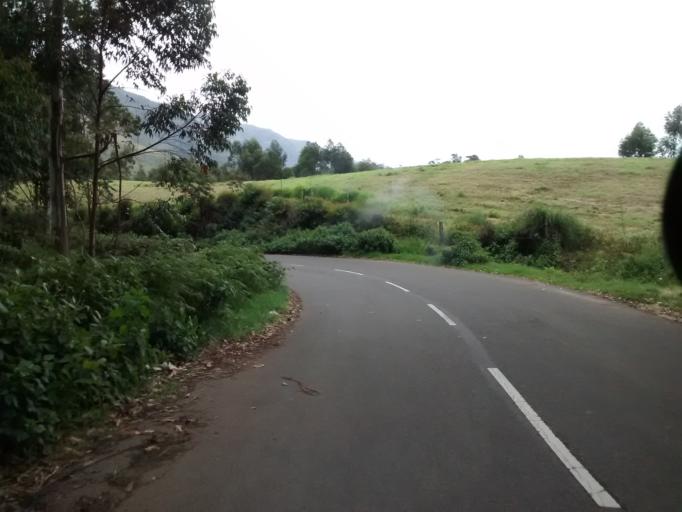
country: IN
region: Kerala
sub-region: Idukki
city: Munnar
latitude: 10.1204
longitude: 77.1459
